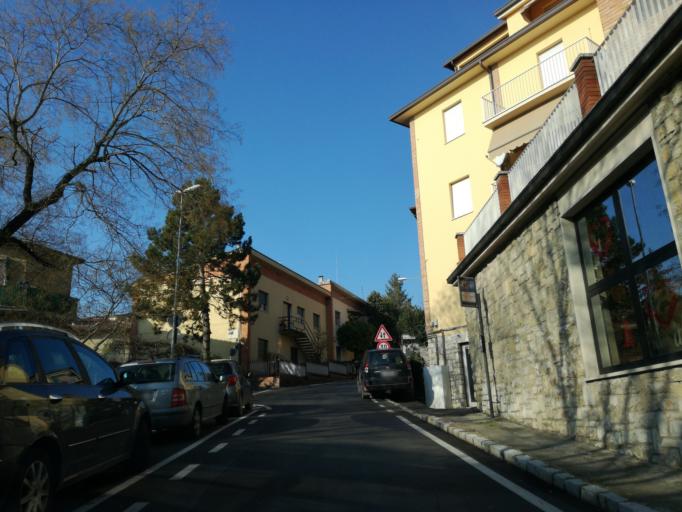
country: IT
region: Umbria
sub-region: Provincia di Perugia
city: Perugia
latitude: 43.1084
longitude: 12.3750
